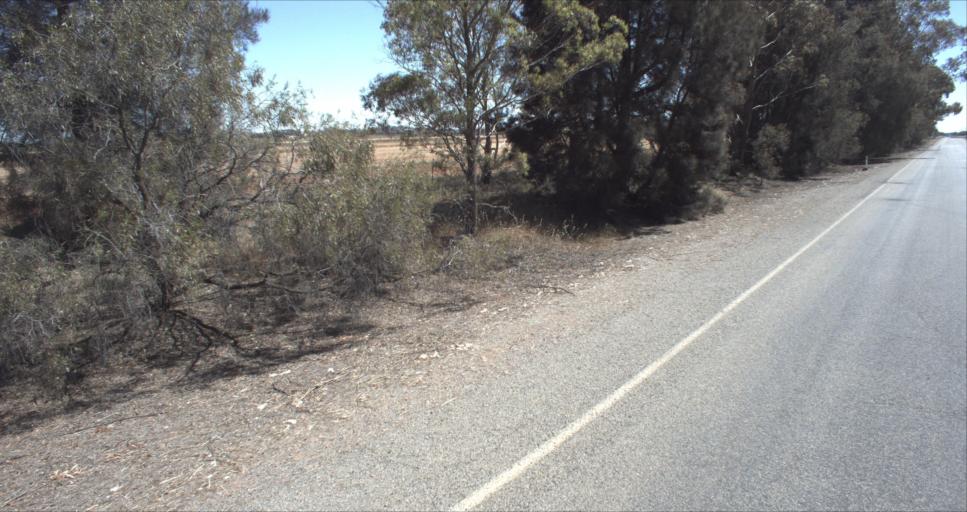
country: AU
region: New South Wales
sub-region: Leeton
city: Leeton
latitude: -34.4675
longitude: 146.2930
